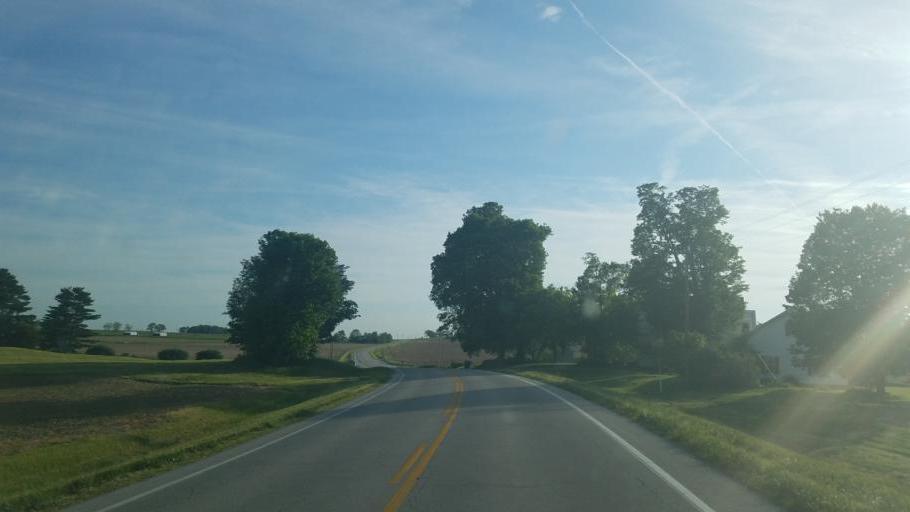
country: US
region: Ohio
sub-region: Highland County
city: Greenfield
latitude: 39.4014
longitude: -83.3118
